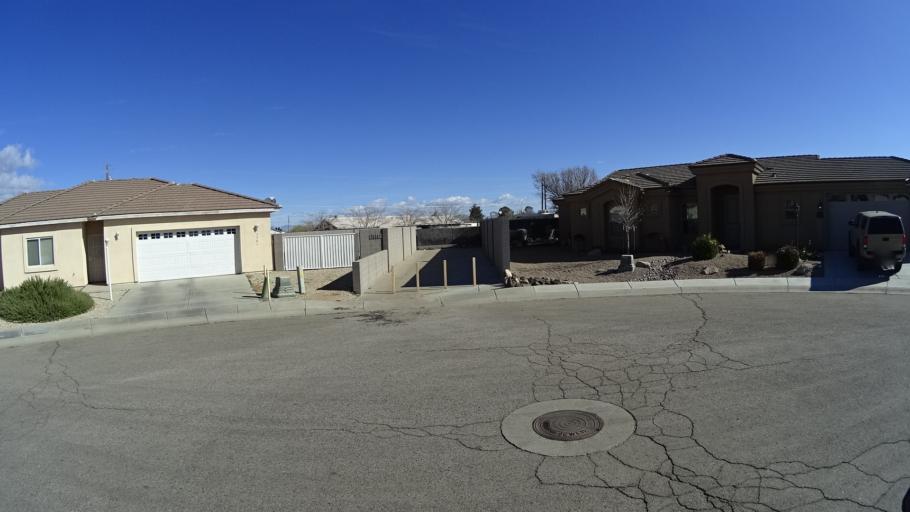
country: US
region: Arizona
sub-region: Mohave County
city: New Kingman-Butler
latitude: 35.2355
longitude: -114.0218
